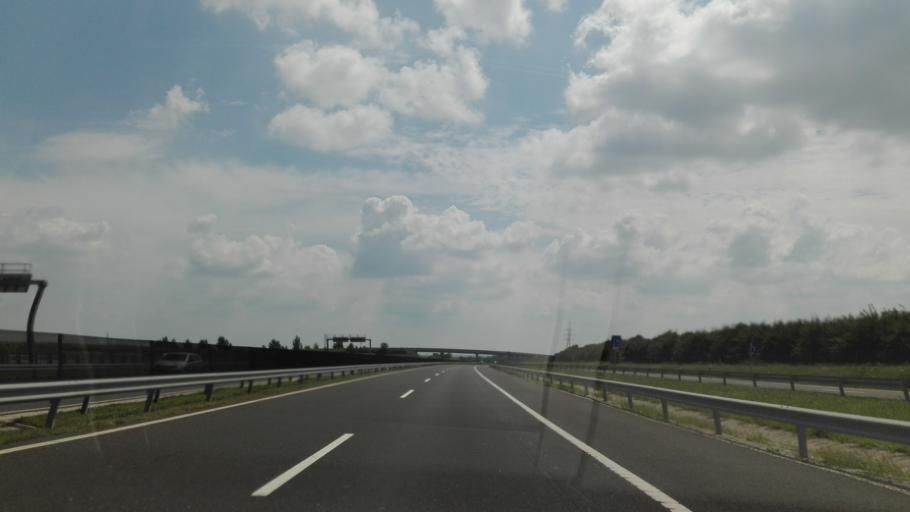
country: HU
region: Fejer
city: dunaujvaros
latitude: 46.9620
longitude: 18.8920
